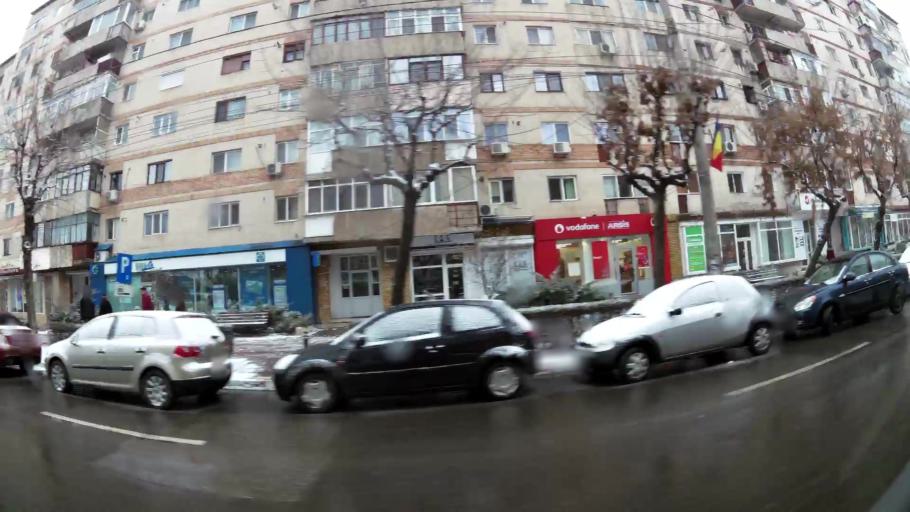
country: RO
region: Dambovita
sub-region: Municipiul Targoviste
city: Targoviste
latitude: 44.9232
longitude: 25.4660
